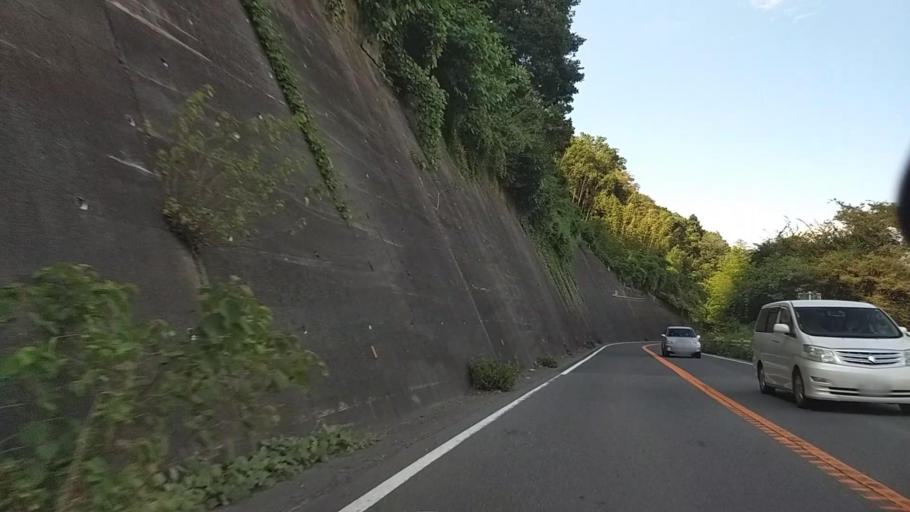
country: JP
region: Shizuoka
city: Fujinomiya
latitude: 35.3974
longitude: 138.4415
